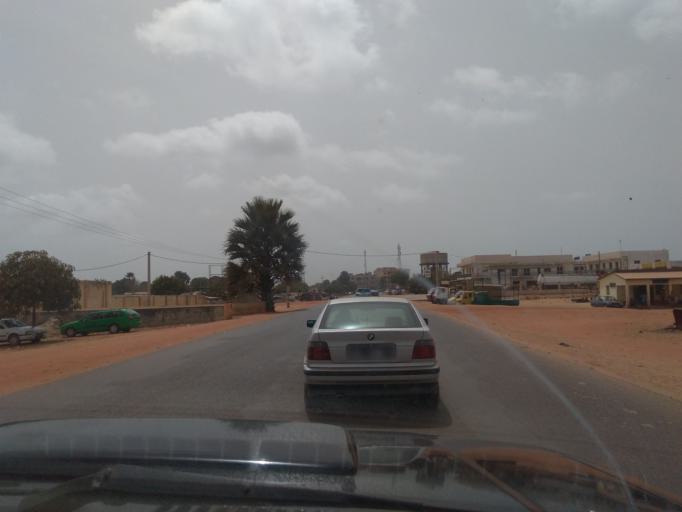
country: GM
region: Western
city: Sukuta
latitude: 13.4413
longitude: -16.7064
